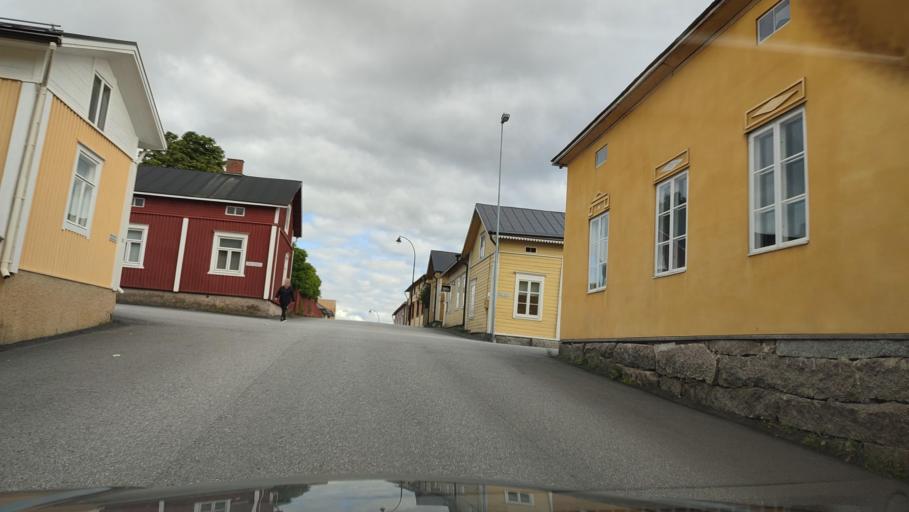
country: FI
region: Ostrobothnia
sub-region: Sydosterbotten
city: Kristinestad
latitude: 62.2756
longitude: 21.3758
